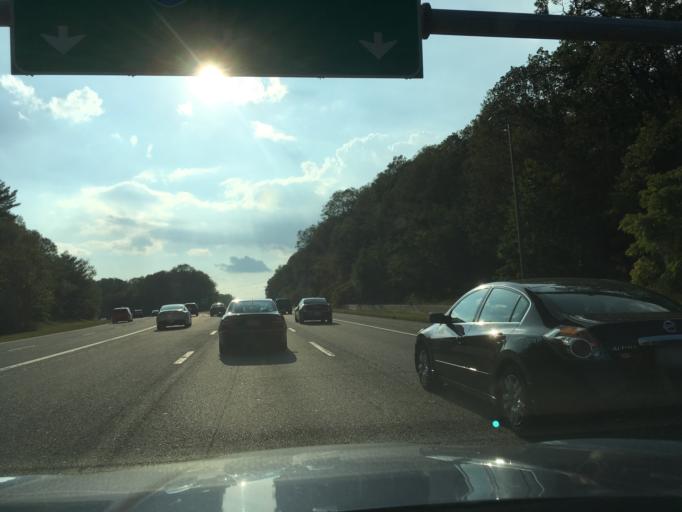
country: US
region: Rhode Island
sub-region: Kent County
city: East Greenwich
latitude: 41.6685
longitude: -71.4868
